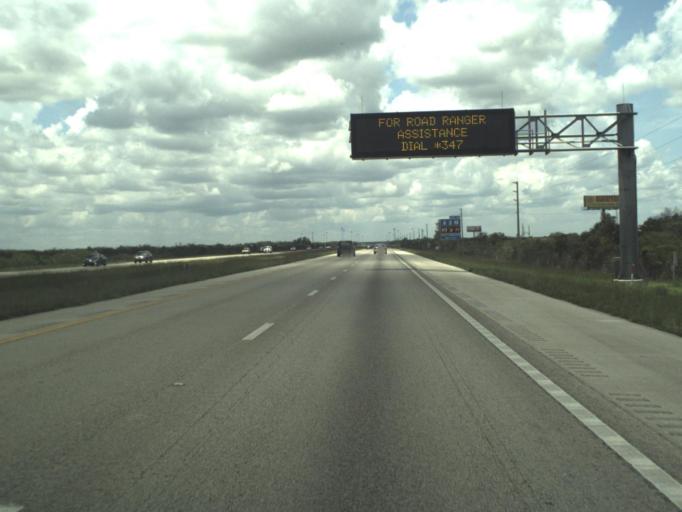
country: US
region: Florida
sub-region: Broward County
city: Weston
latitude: 26.1679
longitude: -80.8367
